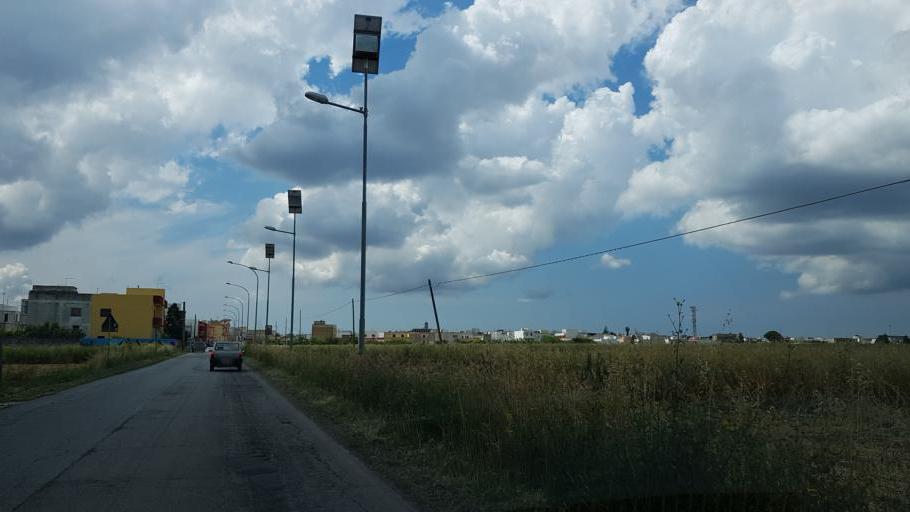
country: IT
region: Apulia
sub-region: Provincia di Brindisi
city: San Pancrazio Salentino
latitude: 40.4264
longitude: 17.8408
